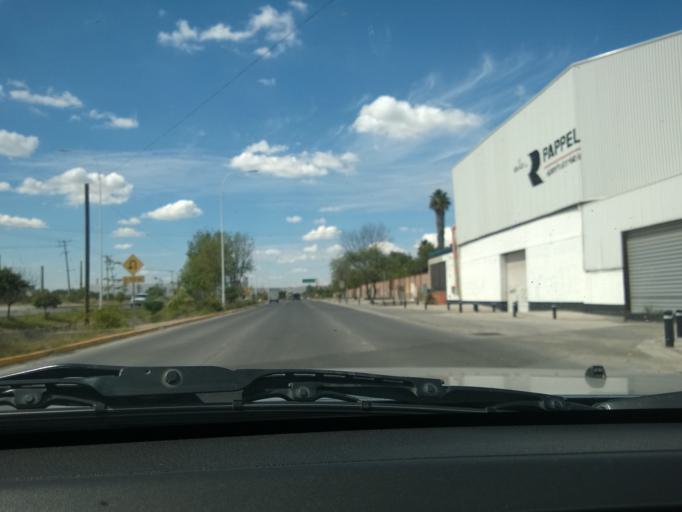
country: MX
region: Guanajuato
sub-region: Leon
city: San Jose de Duran (Los Troncoso)
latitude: 21.0817
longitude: -101.6609
